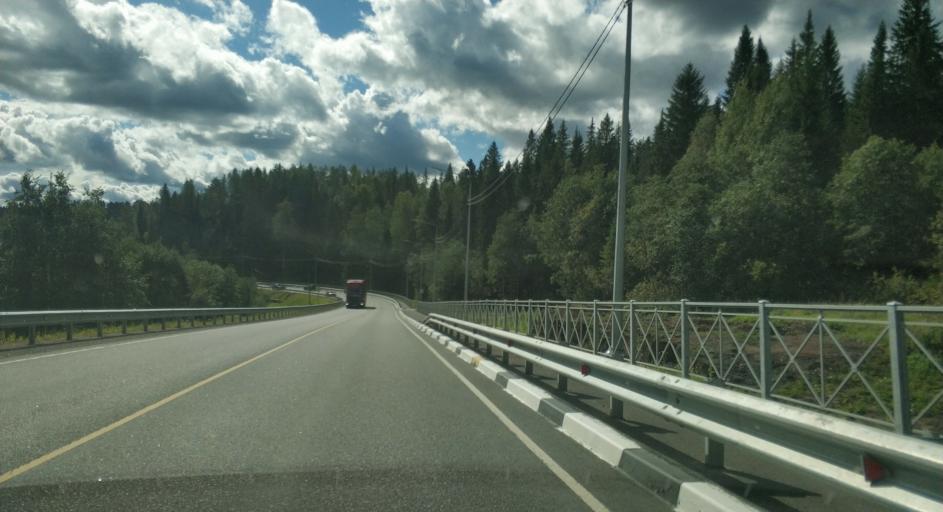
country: RU
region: Republic of Karelia
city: Ruskeala
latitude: 61.9426
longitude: 30.5933
